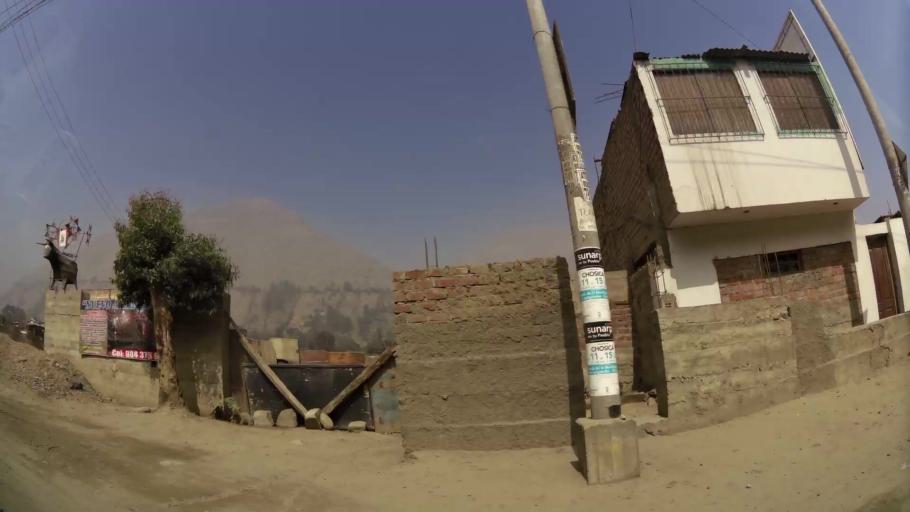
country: PE
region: Lima
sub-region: Provincia de Huarochiri
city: Ricardo Palma
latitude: -11.9239
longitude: -76.6801
